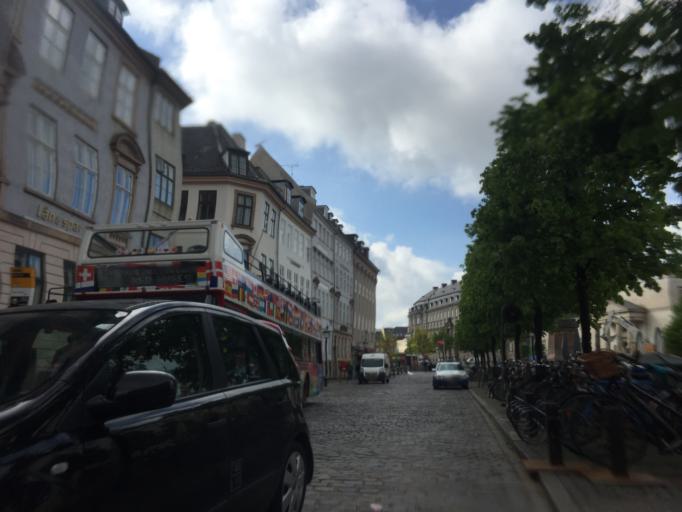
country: DK
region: Capital Region
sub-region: Kobenhavn
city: Copenhagen
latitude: 55.6786
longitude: 12.5799
